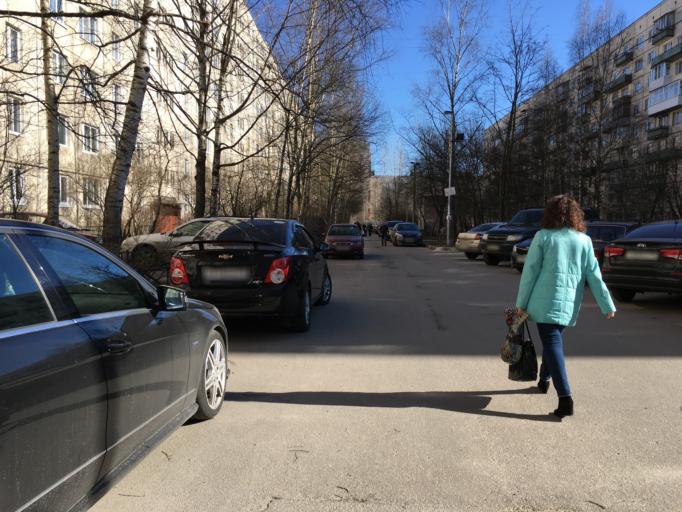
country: RU
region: St.-Petersburg
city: Obukhovo
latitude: 59.9069
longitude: 30.4646
